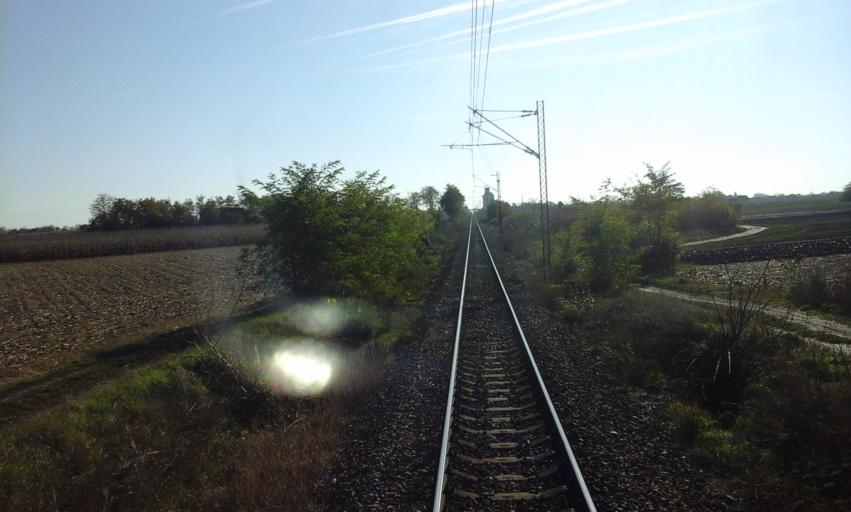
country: RS
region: Autonomna Pokrajina Vojvodina
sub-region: Severnobacki Okrug
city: Subotica
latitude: 45.9564
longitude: 19.6709
